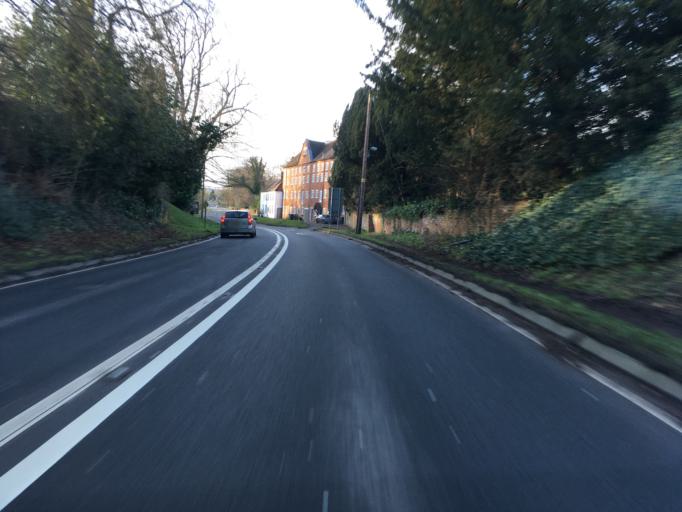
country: GB
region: England
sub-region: Warwickshire
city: Henley in Arden
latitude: 52.2658
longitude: -1.7708
